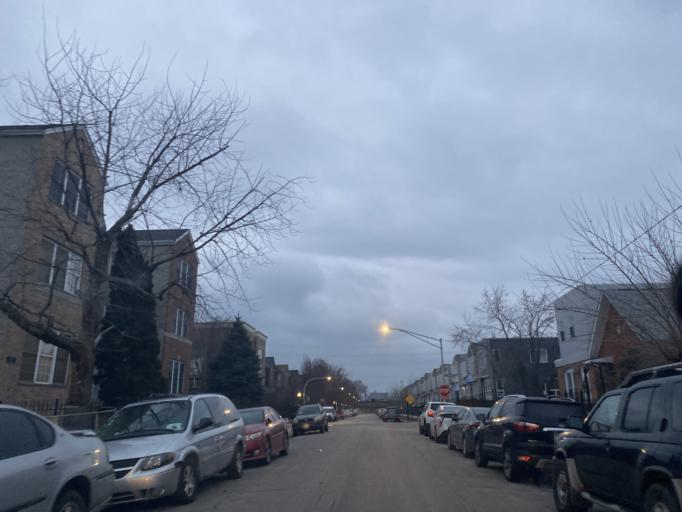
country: US
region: Illinois
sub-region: Cook County
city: Chicago
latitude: 41.8675
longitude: -87.6879
